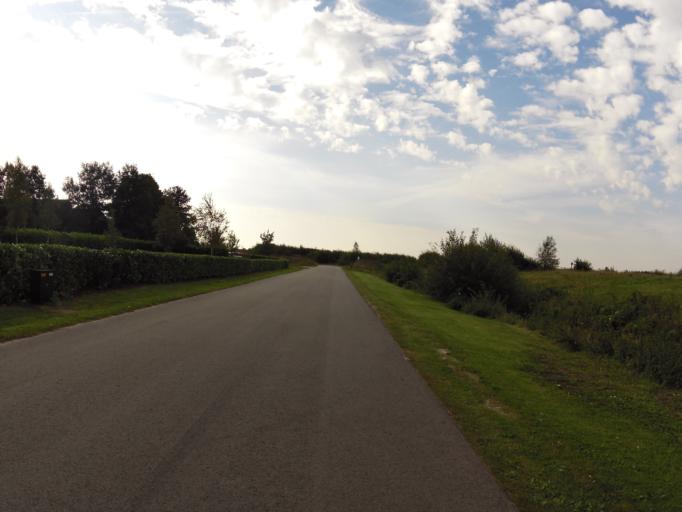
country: NL
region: Drenthe
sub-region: Gemeente Emmen
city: Klazienaveen
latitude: 52.7021
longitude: 7.0449
